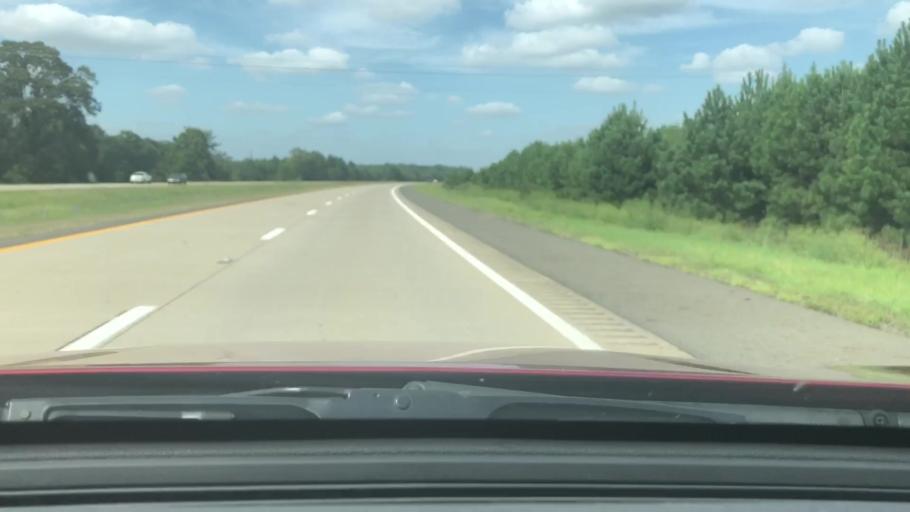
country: US
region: Texas
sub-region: Cass County
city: Queen City
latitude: 33.1983
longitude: -93.8776
